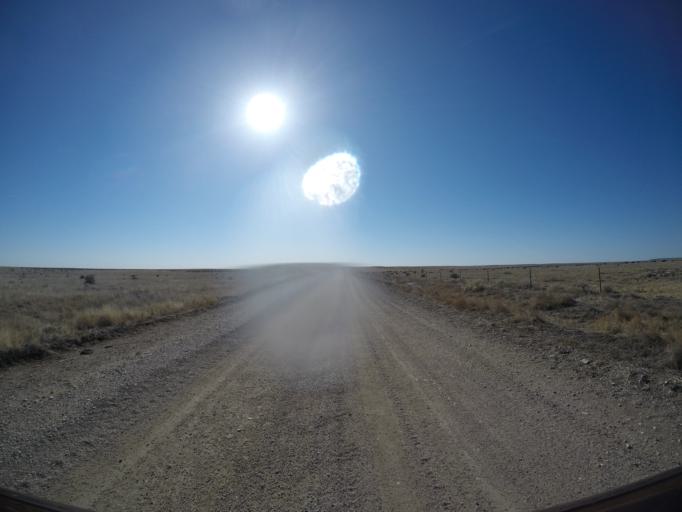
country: US
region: Colorado
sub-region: Otero County
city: La Junta
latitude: 37.7051
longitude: -103.6204
